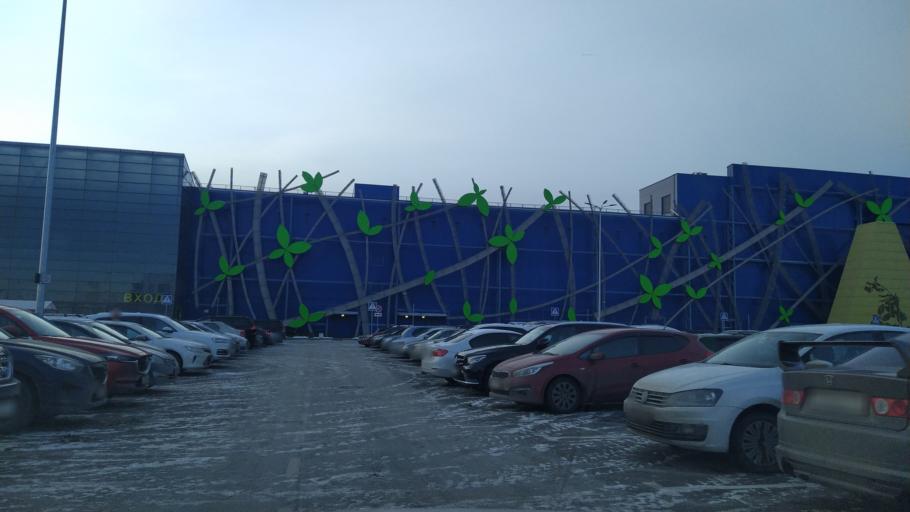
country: RU
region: St.-Petersburg
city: Kupchino
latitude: 59.8191
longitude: 30.3199
